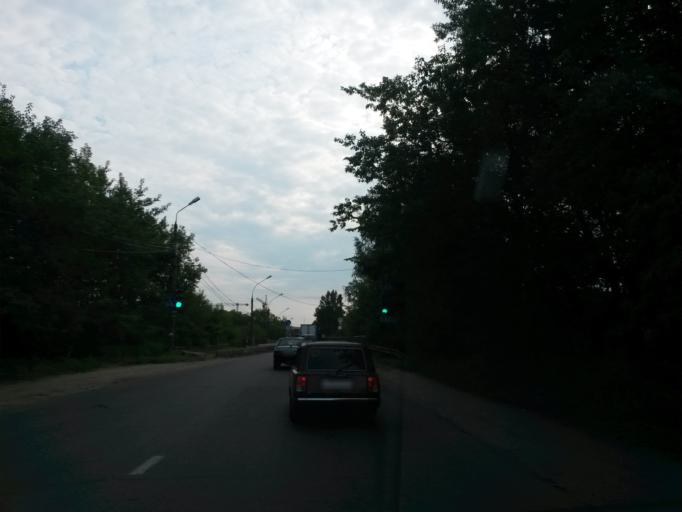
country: RU
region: Jaroslavl
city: Yaroslavl
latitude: 57.6110
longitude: 39.8384
